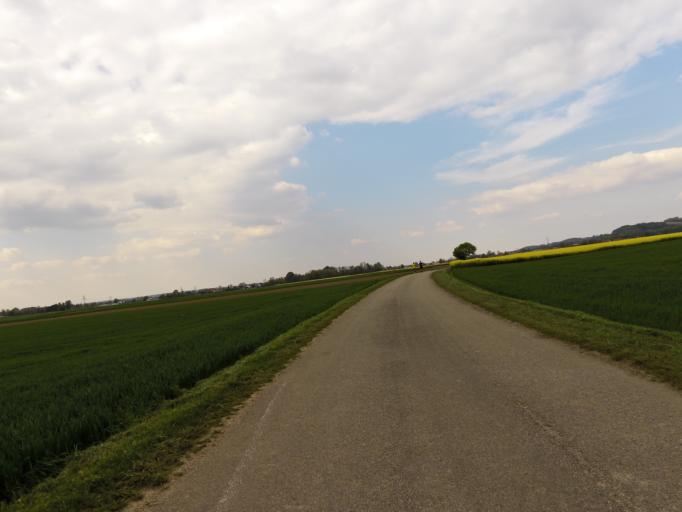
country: DE
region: Bavaria
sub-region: Upper Bavaria
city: Langenpreising
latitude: 48.4126
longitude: 11.9623
